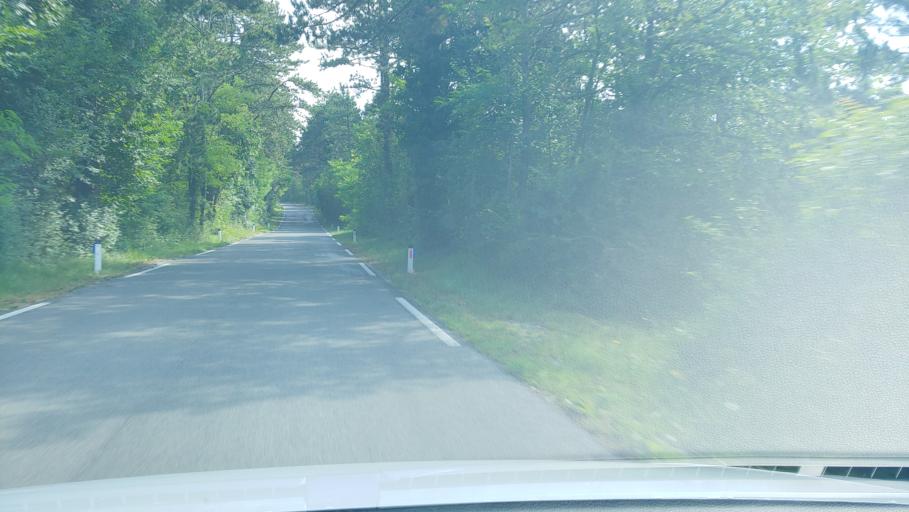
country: SI
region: Komen
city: Komen
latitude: 45.8274
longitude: 13.7592
